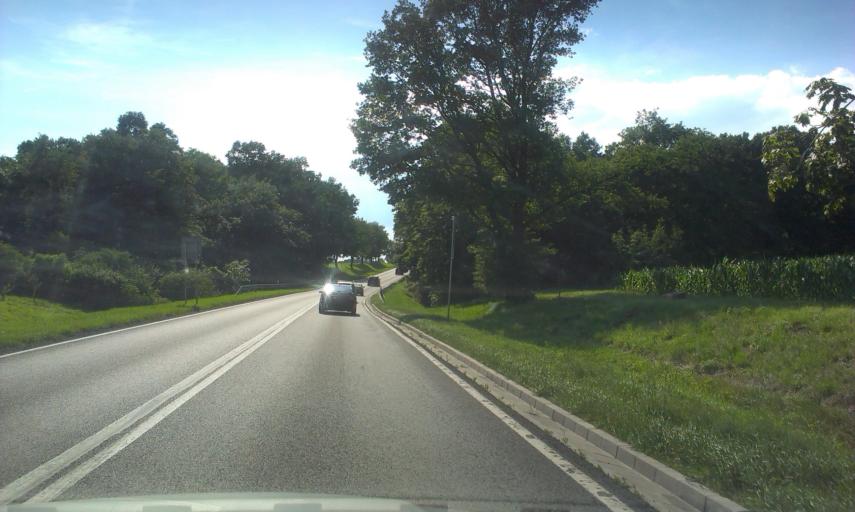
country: PL
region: Kujawsko-Pomorskie
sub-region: Powiat nakielski
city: Slesin
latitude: 53.1674
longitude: 17.7573
